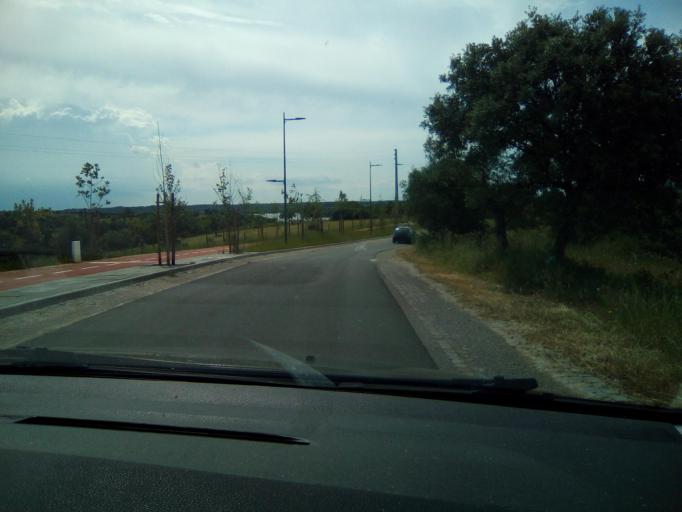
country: PT
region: Portalegre
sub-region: Avis
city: Avis
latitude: 39.0549
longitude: -7.9066
